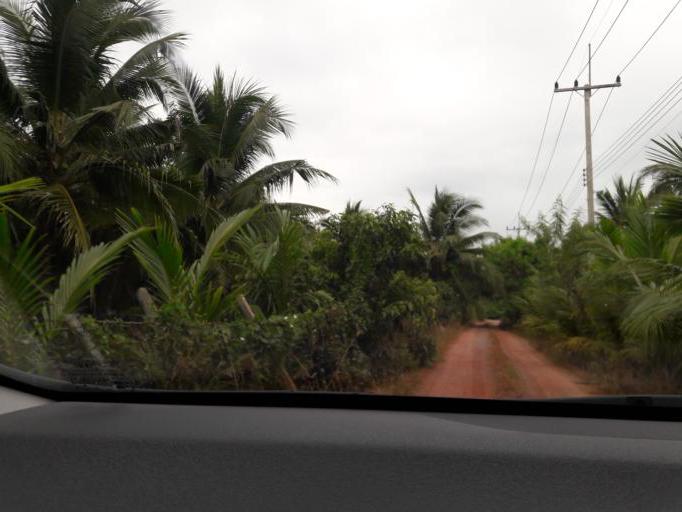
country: TH
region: Ratchaburi
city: Damnoen Saduak
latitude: 13.5696
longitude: 100.0168
